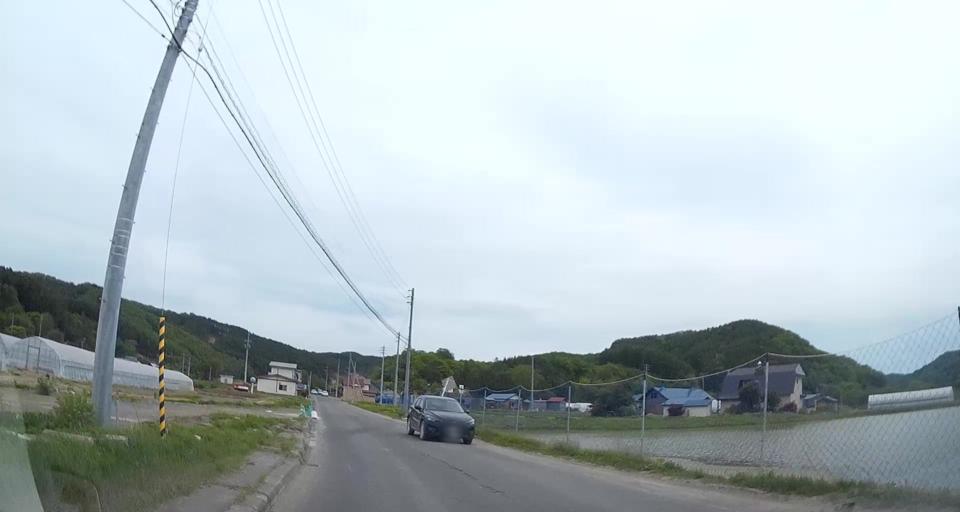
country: JP
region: Hokkaido
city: Chitose
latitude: 42.7551
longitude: 141.9746
